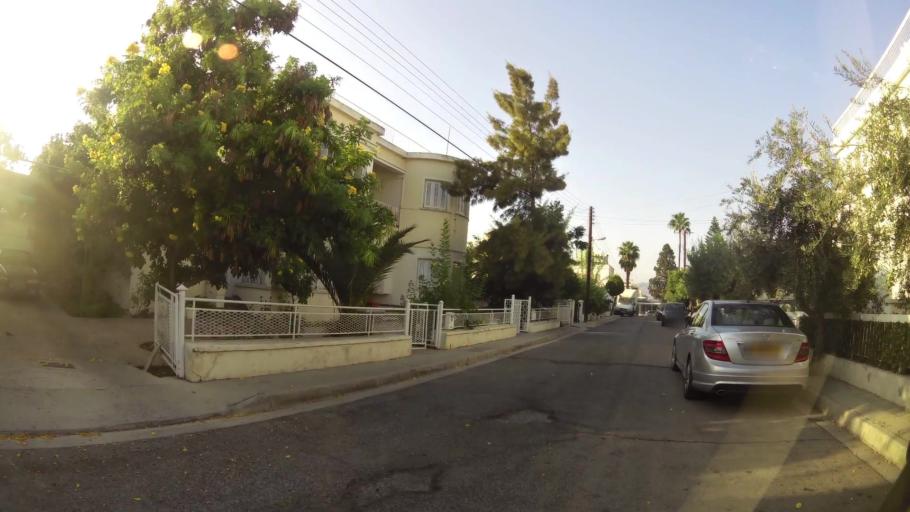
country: CY
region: Lefkosia
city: Nicosia
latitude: 35.1702
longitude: 33.3373
